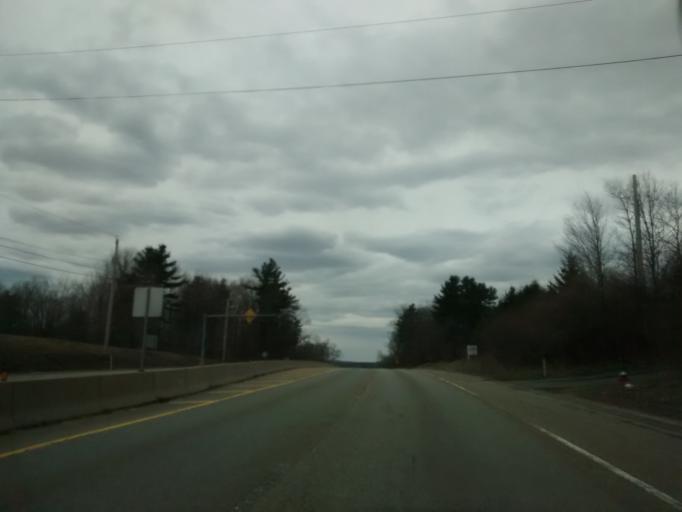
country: US
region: Massachusetts
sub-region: Worcester County
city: Charlton
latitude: 42.1461
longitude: -71.9708
